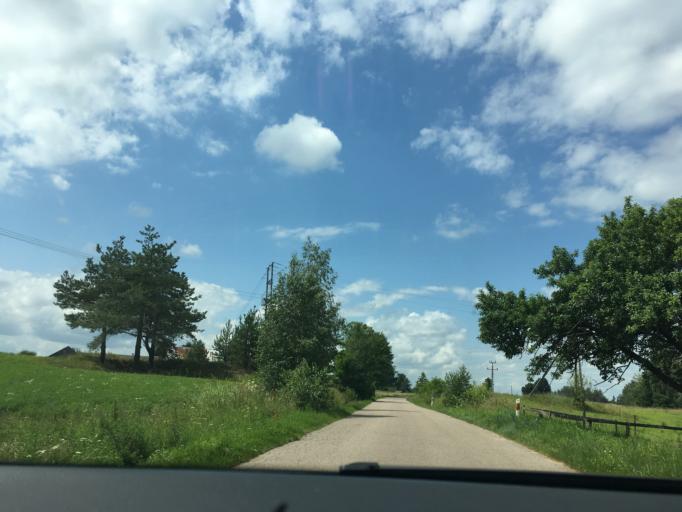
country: PL
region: Podlasie
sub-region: Powiat sejnenski
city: Krasnopol
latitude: 54.0963
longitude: 23.2296
